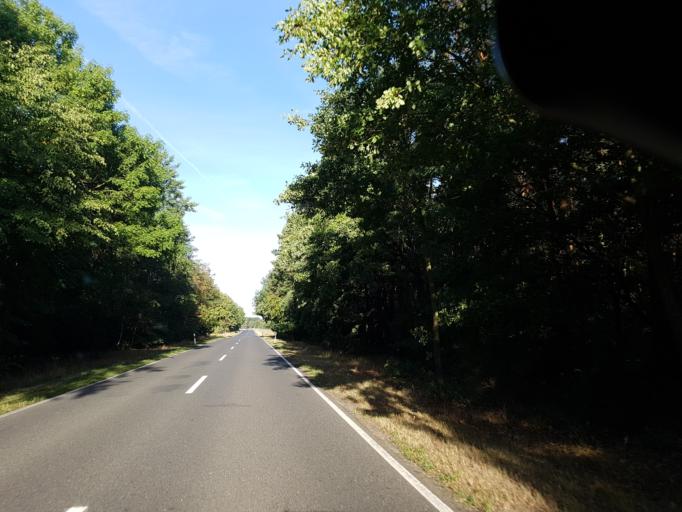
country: DE
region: Brandenburg
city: Elsterwerda
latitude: 51.4689
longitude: 13.4859
